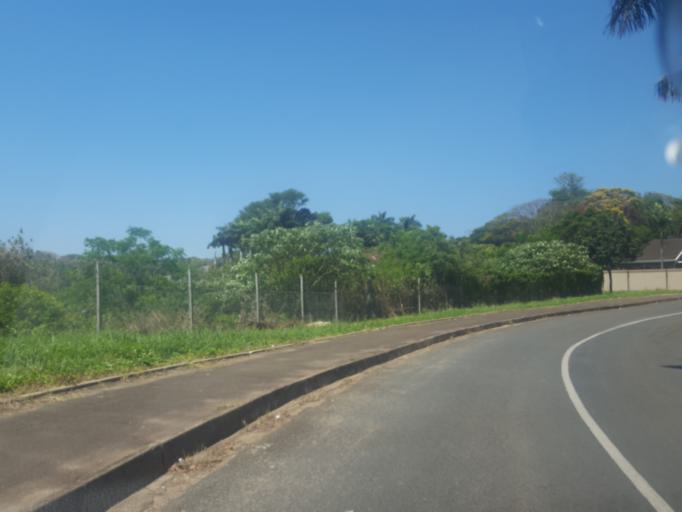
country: ZA
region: KwaZulu-Natal
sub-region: uThungulu District Municipality
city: Empangeni
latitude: -28.7435
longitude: 31.9032
